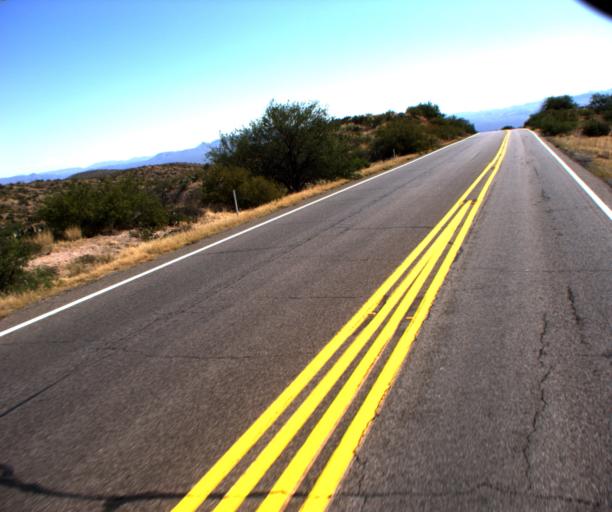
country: US
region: Arizona
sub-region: Pinal County
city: Oracle
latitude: 32.6475
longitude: -110.7162
